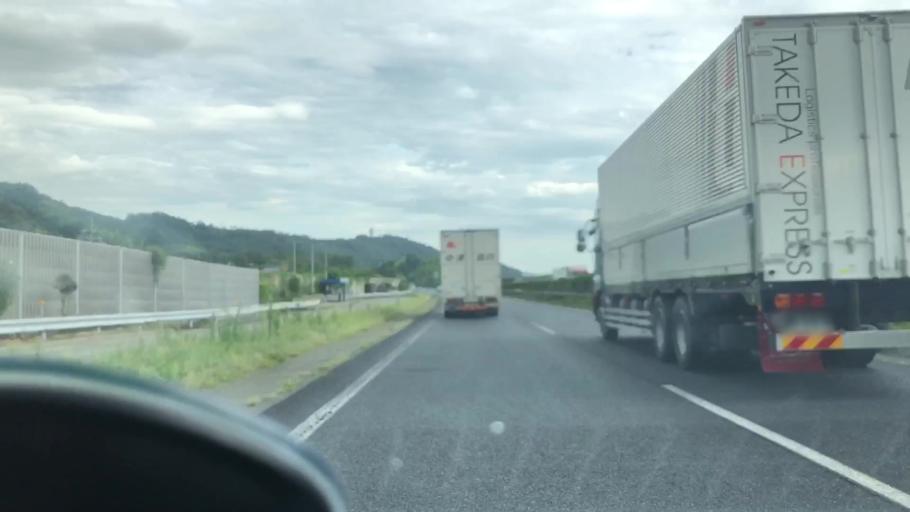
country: JP
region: Hyogo
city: Ono
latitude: 34.9356
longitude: 134.8361
